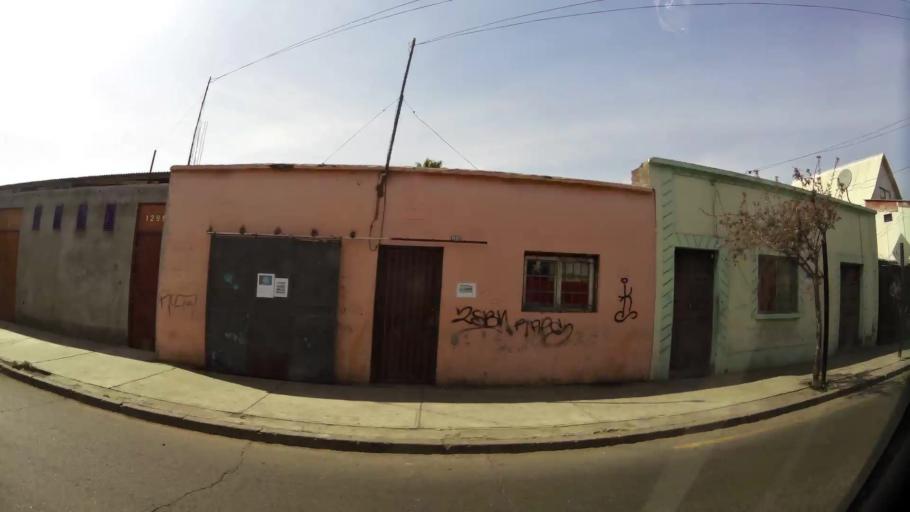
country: CL
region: Santiago Metropolitan
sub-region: Provincia de Santiago
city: Lo Prado
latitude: -33.4349
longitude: -70.7670
